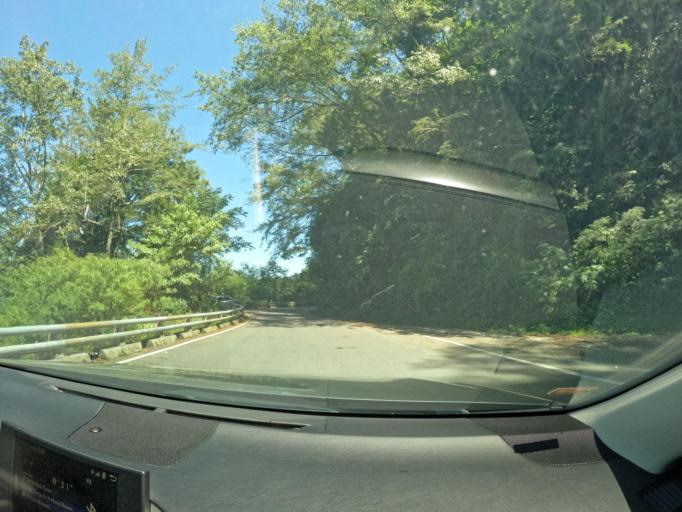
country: TW
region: Taiwan
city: Yujing
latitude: 23.2788
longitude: 120.8937
